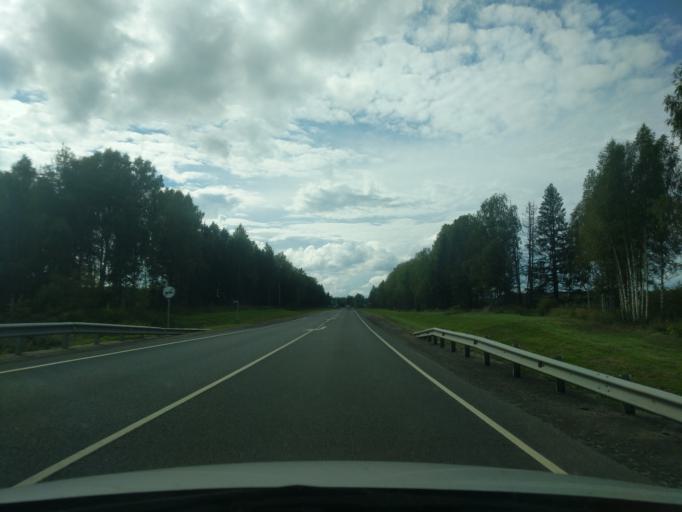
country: RU
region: Jaroslavl
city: Nekrasovskoye
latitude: 57.6352
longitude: 40.4208
